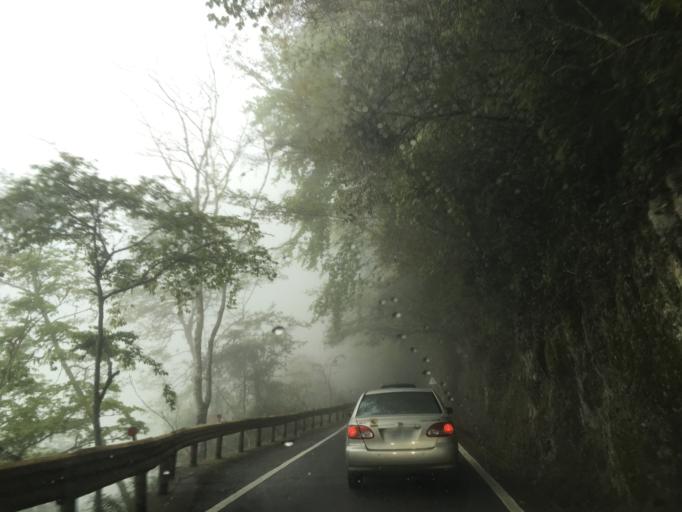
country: TW
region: Taiwan
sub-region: Hualien
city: Hualian
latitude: 24.1864
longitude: 121.4148
